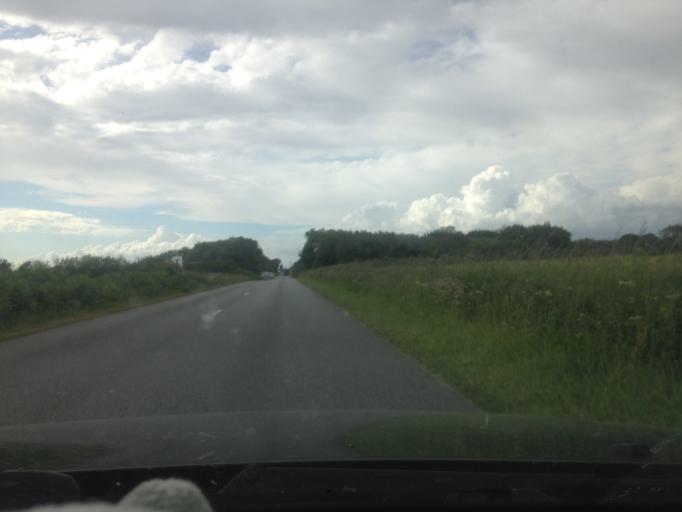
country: FR
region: Brittany
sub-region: Departement du Morbihan
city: Erdeven
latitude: 47.6227
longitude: -3.1373
